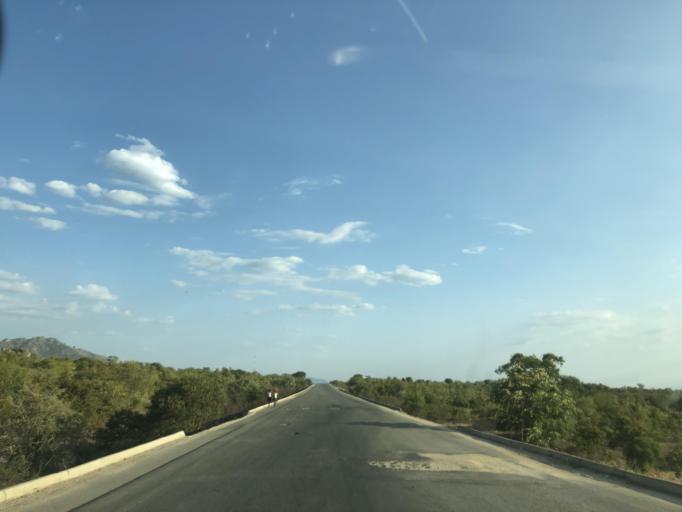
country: AO
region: Huila
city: Caluquembe
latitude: -13.5066
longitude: 13.9181
